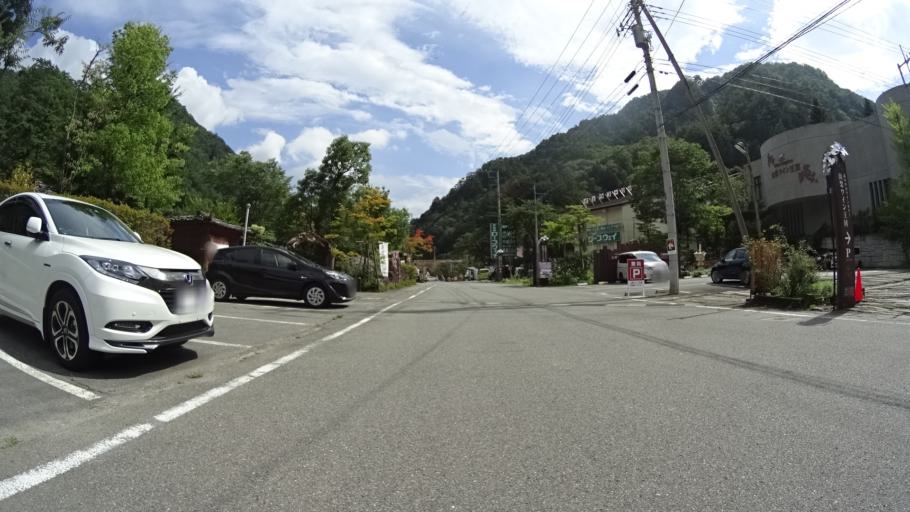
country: JP
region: Yamanashi
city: Kofu-shi
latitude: 35.7541
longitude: 138.5645
